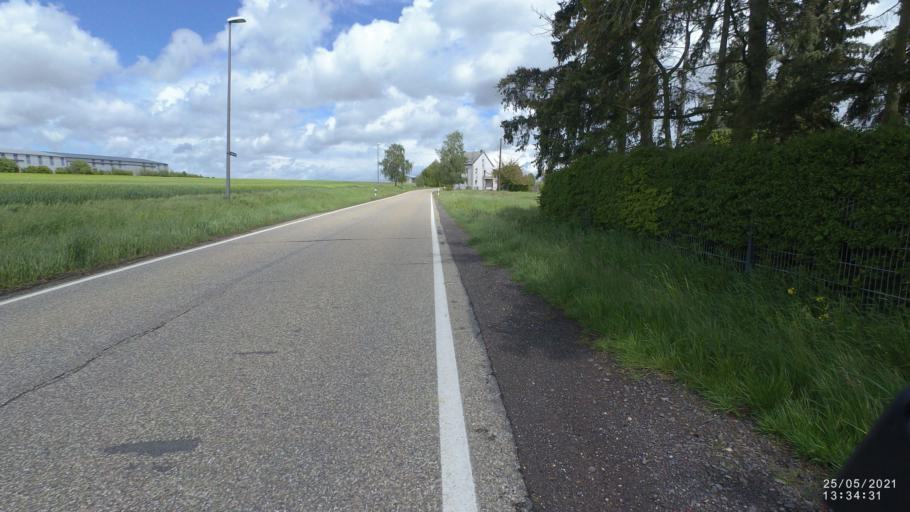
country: DE
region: Rheinland-Pfalz
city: Kehrig
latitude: 50.2842
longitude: 7.2229
